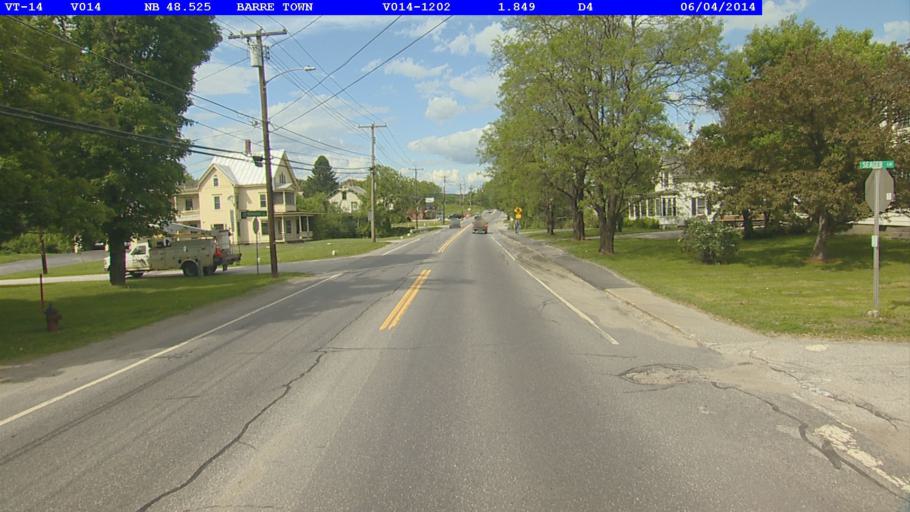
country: US
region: Vermont
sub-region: Washington County
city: South Barre
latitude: 44.1755
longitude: -72.5062
